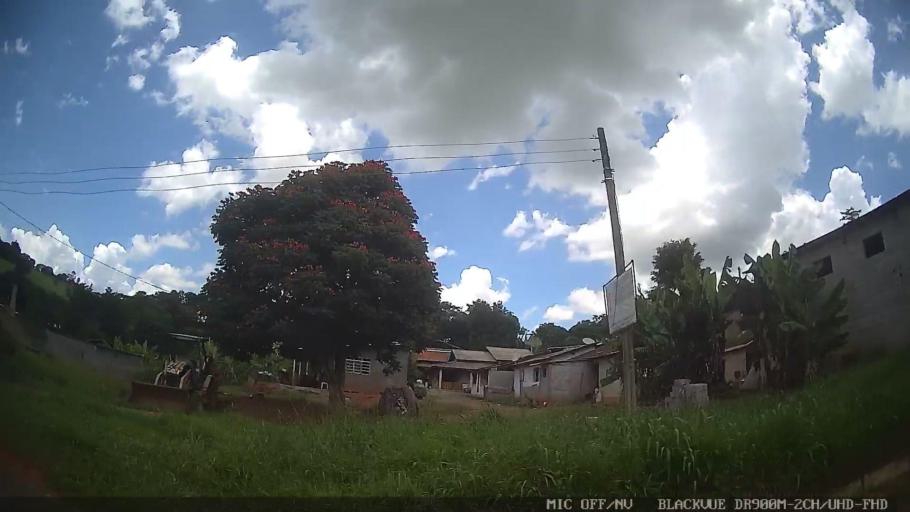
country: BR
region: Sao Paulo
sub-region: Braganca Paulista
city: Braganca Paulista
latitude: -23.0170
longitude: -46.4931
